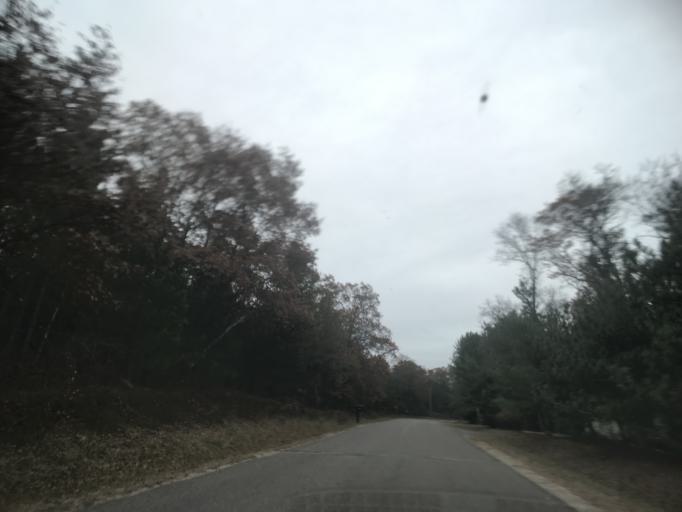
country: US
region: Wisconsin
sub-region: Oconto County
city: Gillett
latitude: 45.2697
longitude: -88.2550
